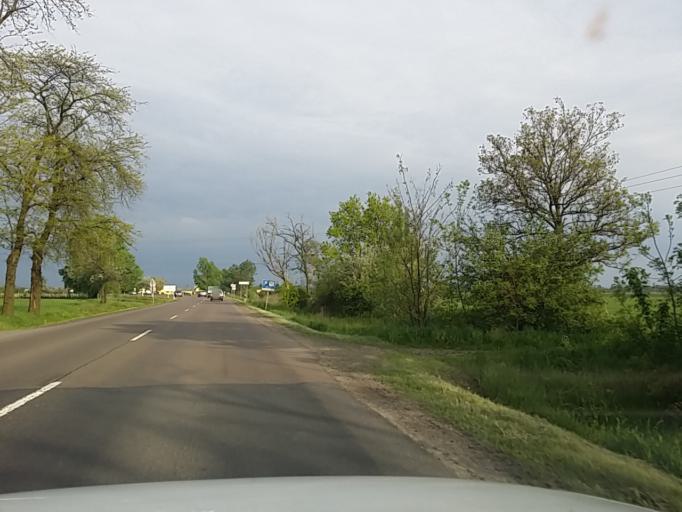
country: HU
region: Jasz-Nagykun-Szolnok
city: Jaszbereny
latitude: 47.5173
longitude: 19.8769
